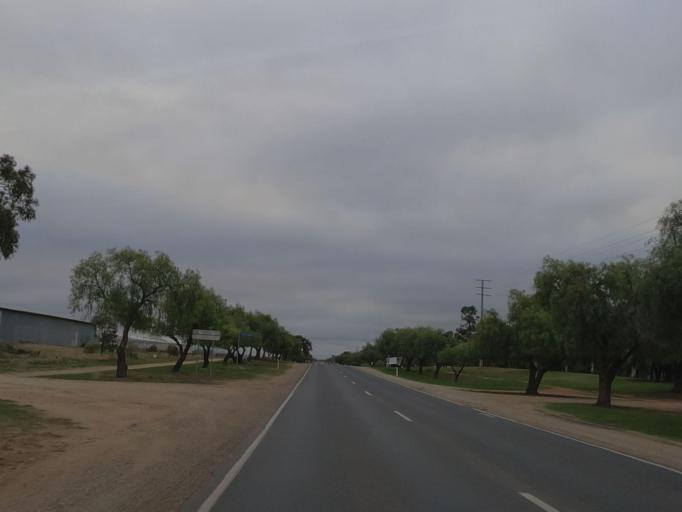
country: AU
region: Victoria
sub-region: Swan Hill
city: Swan Hill
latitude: -35.4560
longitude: 143.6291
